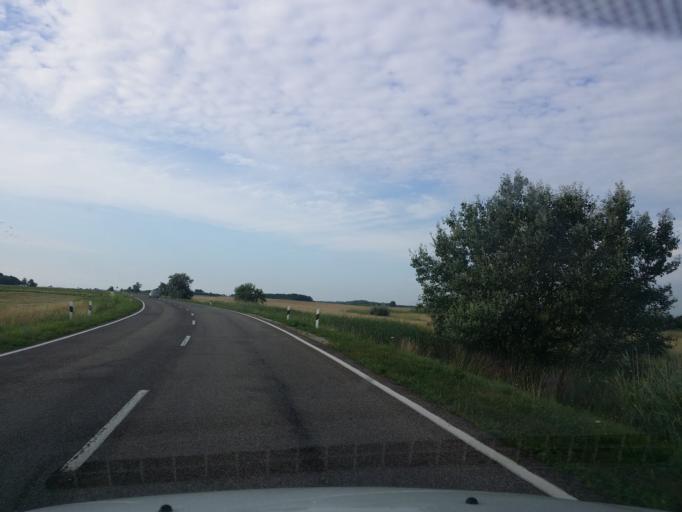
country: HU
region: Hajdu-Bihar
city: Egyek
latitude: 47.5803
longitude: 20.8542
